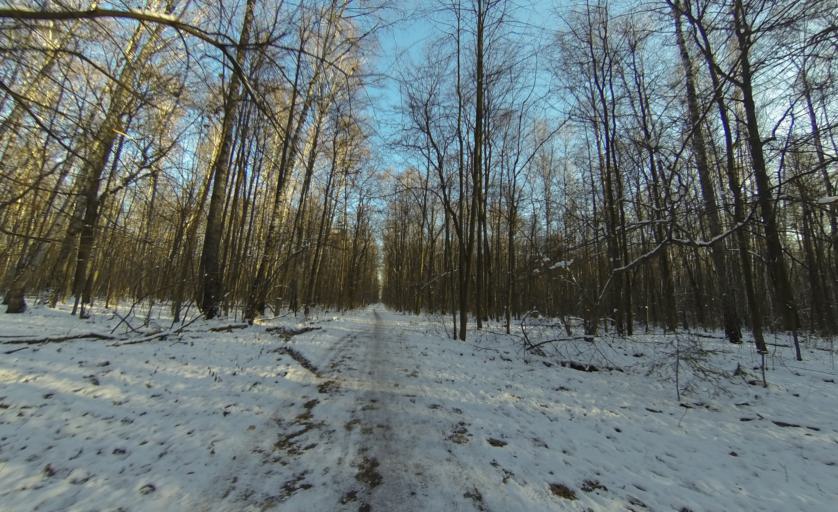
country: RU
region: Moscow
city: Rostokino
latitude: 55.8255
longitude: 37.6867
